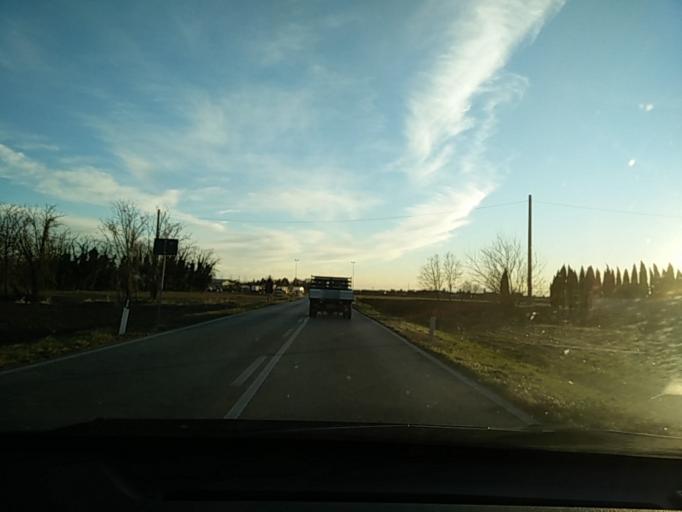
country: IT
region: Friuli Venezia Giulia
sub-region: Provincia di Udine
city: Lestizza
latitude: 45.9683
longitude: 13.1121
